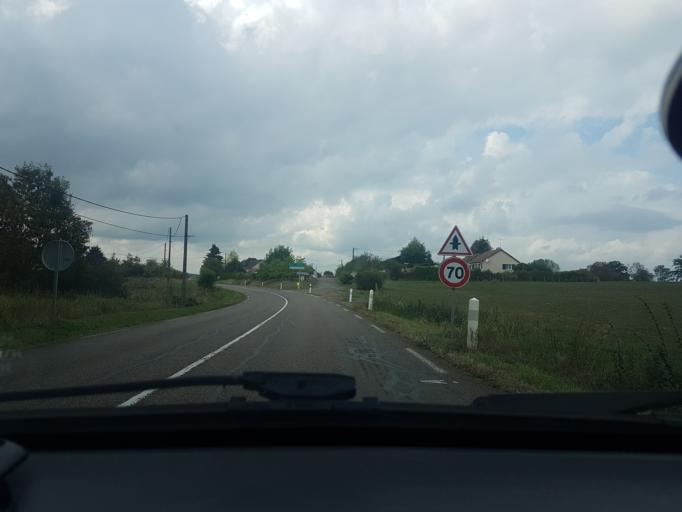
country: FR
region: Franche-Comte
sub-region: Departement de la Haute-Saone
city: Villersexel
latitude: 47.5427
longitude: 6.5149
